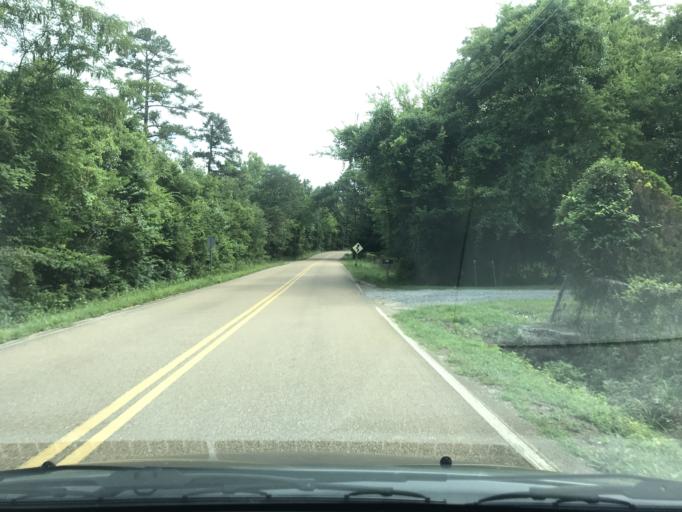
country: US
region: Tennessee
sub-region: Hamilton County
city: Lakesite
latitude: 35.2033
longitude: -85.0987
